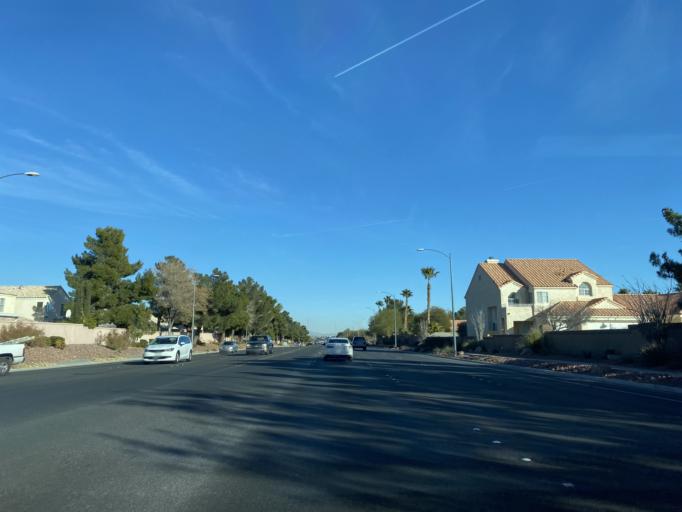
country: US
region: Nevada
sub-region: Clark County
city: Las Vegas
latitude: 36.2630
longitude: -115.2651
